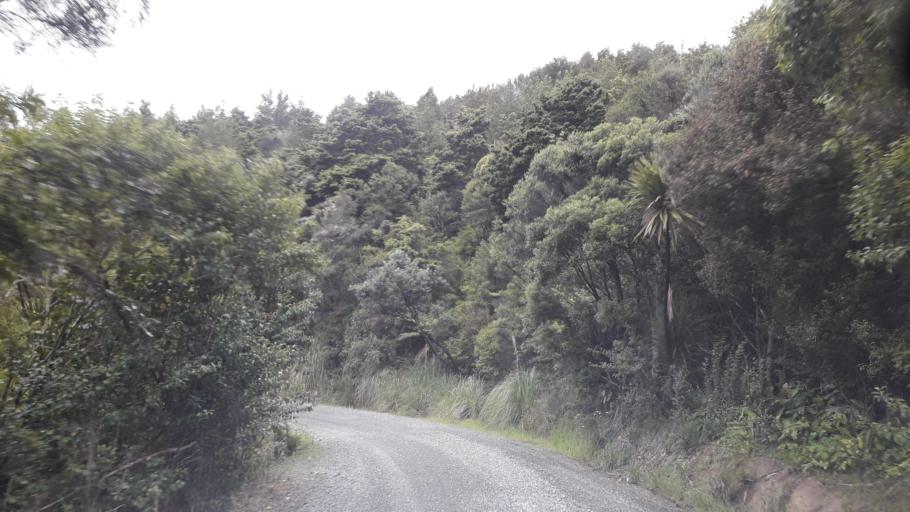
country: NZ
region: Northland
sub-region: Far North District
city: Waimate North
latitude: -35.3058
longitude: 173.5628
